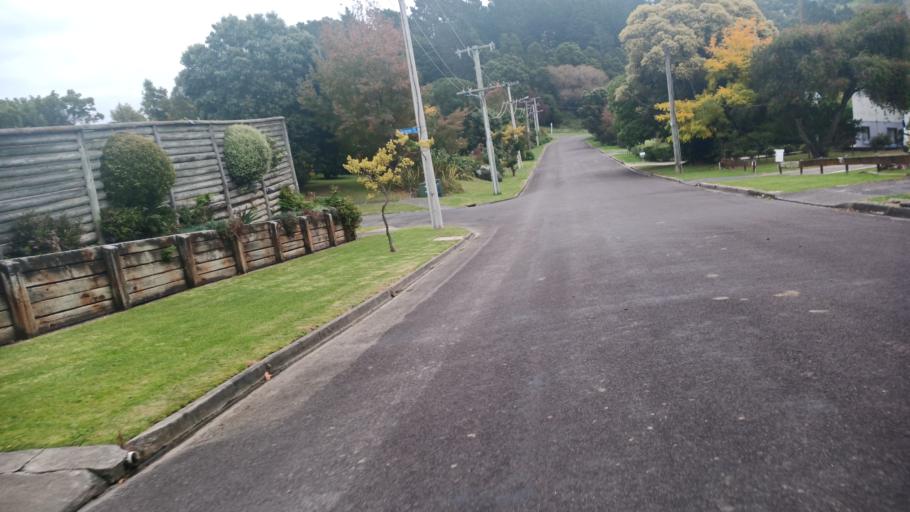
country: NZ
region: Gisborne
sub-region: Gisborne District
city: Gisborne
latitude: -38.6830
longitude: 178.0426
